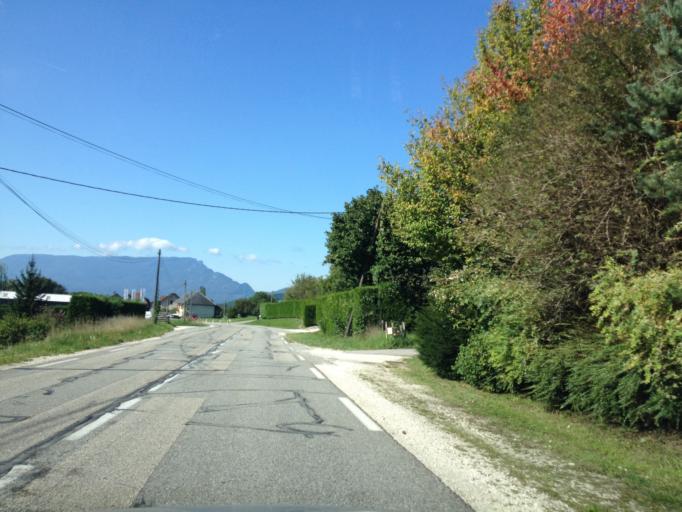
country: FR
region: Rhone-Alpes
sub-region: Departement de la Haute-Savoie
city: Cusy
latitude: 45.7505
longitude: 5.9941
